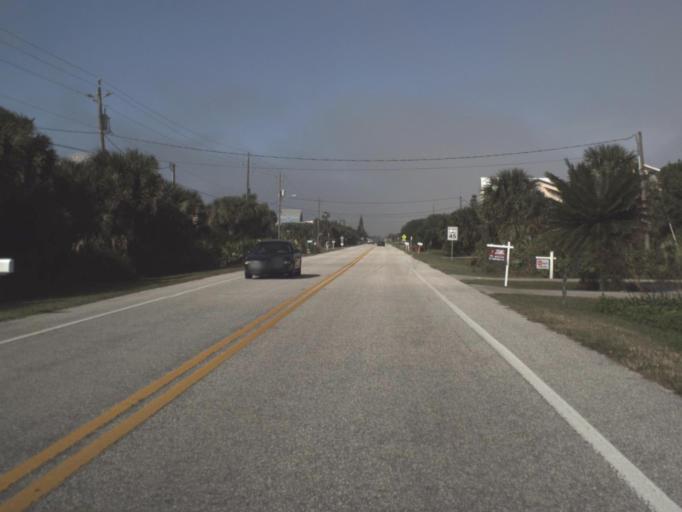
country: US
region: Florida
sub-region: Volusia County
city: Edgewater
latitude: 28.9453
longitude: -80.8361
